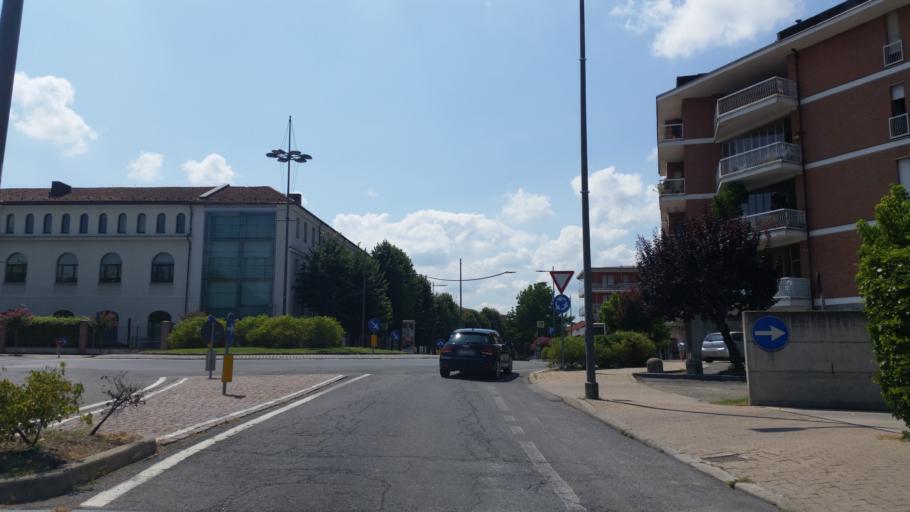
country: IT
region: Piedmont
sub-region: Provincia di Cuneo
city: Alba
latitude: 44.6976
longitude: 8.0274
